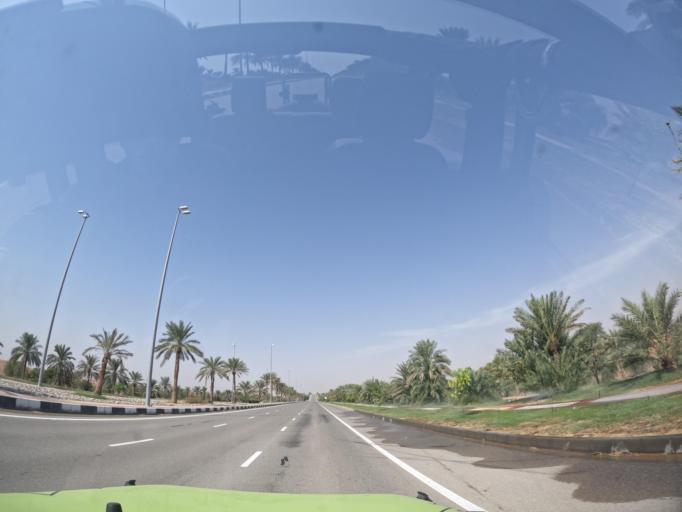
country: AE
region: Abu Dhabi
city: Al Ain
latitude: 24.2611
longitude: 55.6554
